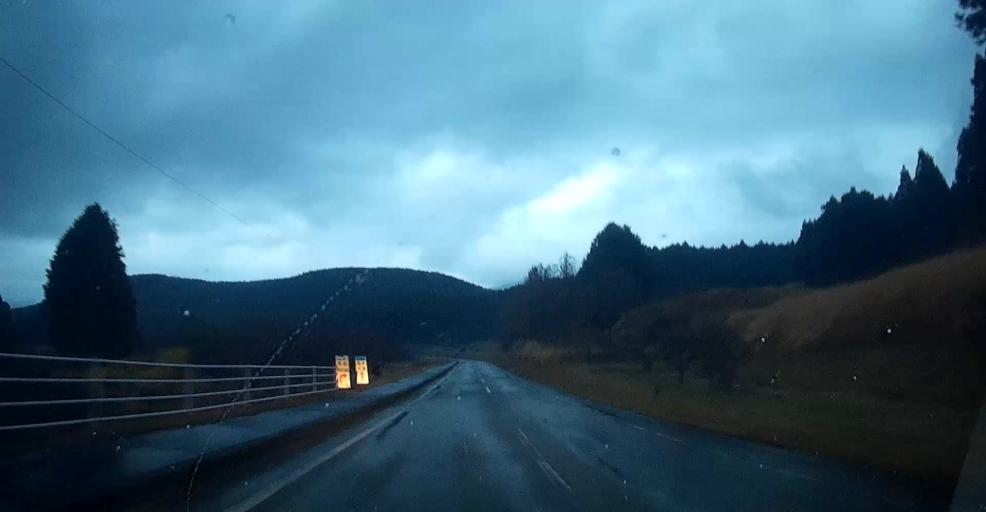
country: JP
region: Kumamoto
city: Ozu
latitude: 32.8295
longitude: 130.9150
